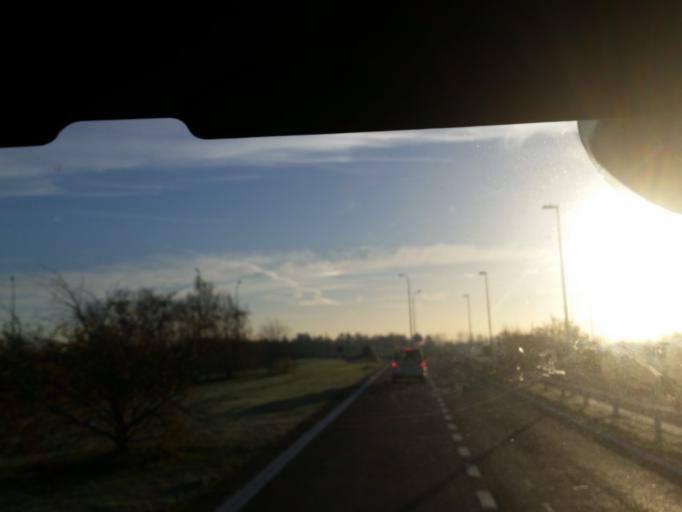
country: BE
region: Flanders
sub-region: Provincie Antwerpen
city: Retie
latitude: 51.2944
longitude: 5.0912
